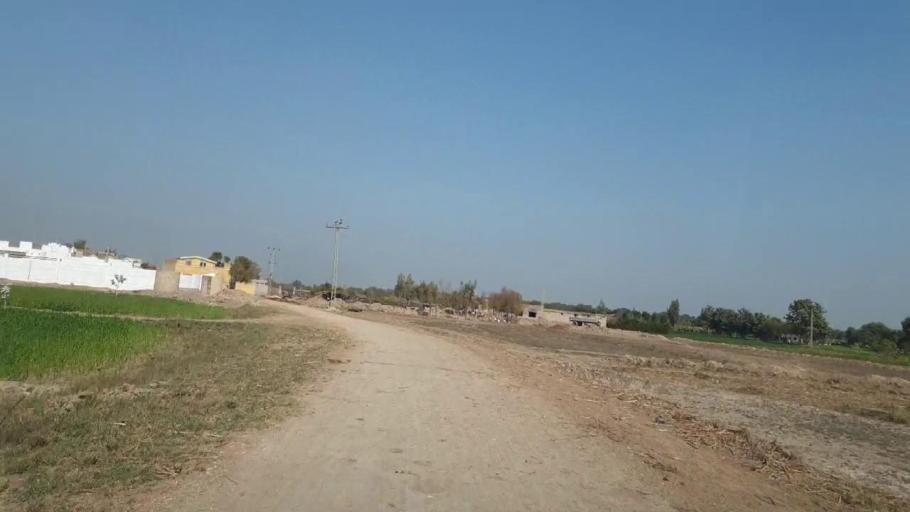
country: PK
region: Sindh
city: Matiari
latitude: 25.5061
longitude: 68.4591
